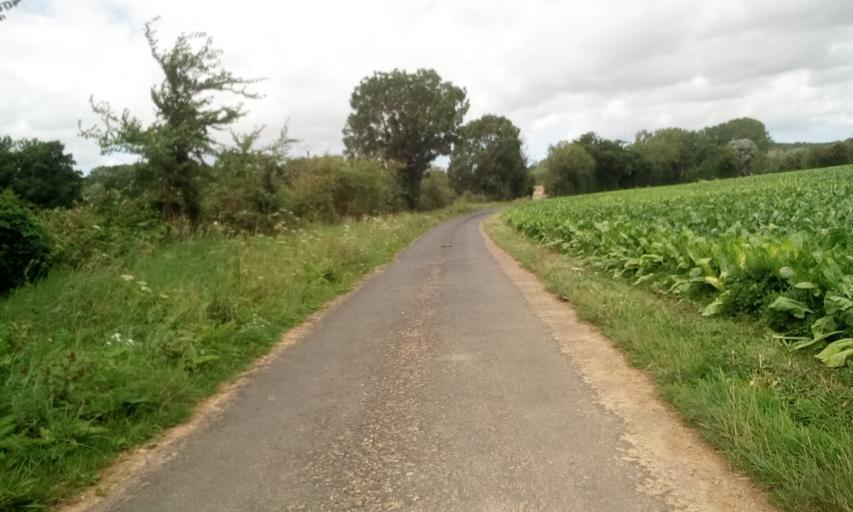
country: FR
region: Lower Normandy
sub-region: Departement du Calvados
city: Tilly-sur-Seulles
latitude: 49.2070
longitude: -0.6295
